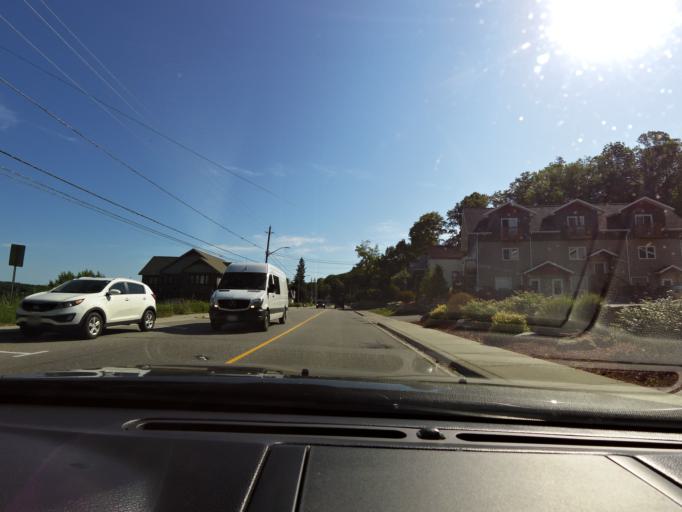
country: CA
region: Ontario
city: Huntsville
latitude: 45.3208
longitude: -79.2289
